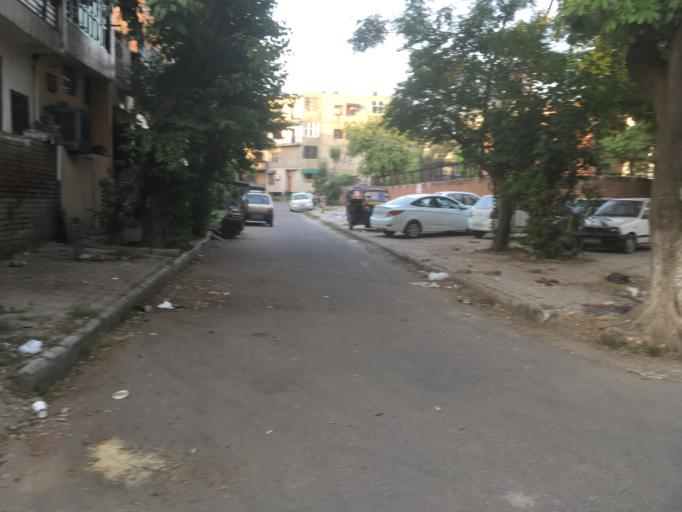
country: IN
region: Chandigarh
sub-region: Chandigarh
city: Chandigarh
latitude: 30.7170
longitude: 76.8300
